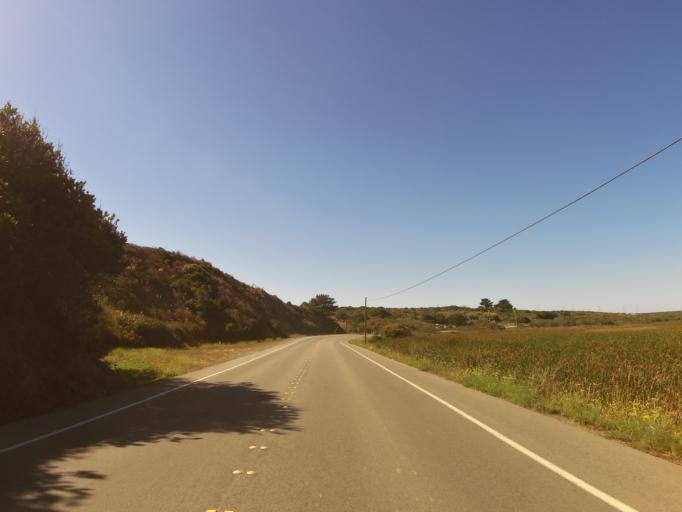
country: US
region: California
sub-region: San Mateo County
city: Half Moon Bay
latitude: 37.2529
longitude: -122.4047
